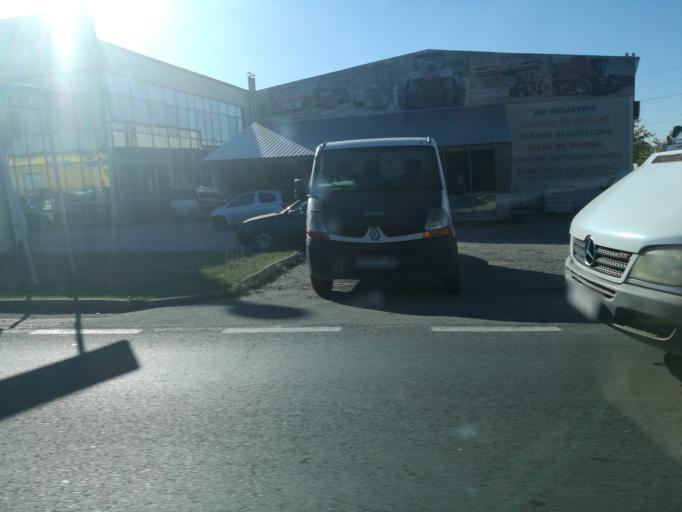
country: RO
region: Brasov
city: Brasov
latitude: 45.6921
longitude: 25.5835
